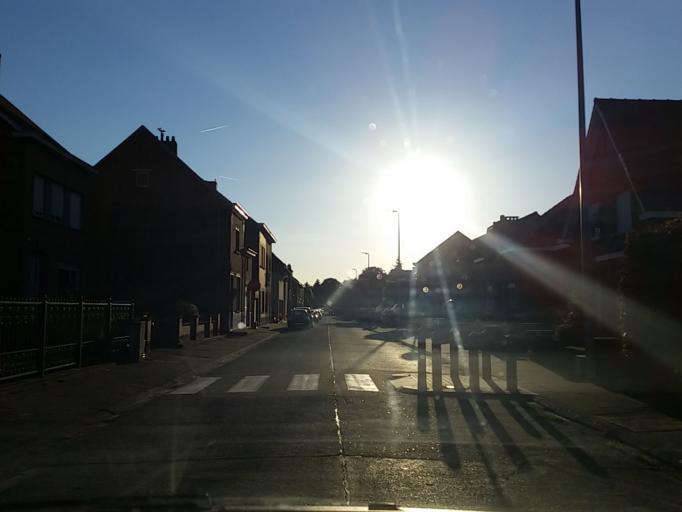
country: BE
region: Flanders
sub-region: Provincie Vlaams-Brabant
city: Steenokkerzeel
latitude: 50.9617
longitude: 4.5016
